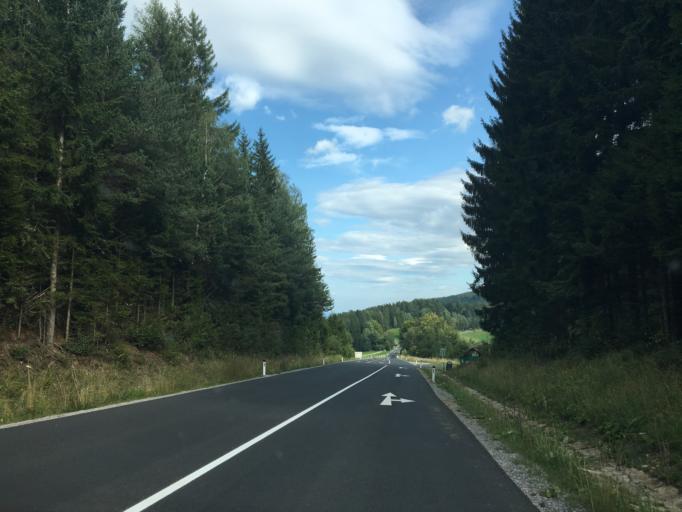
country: AT
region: Styria
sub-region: Politischer Bezirk Deutschlandsberg
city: Freiland bei Deutschlandsberg
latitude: 46.8306
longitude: 15.1104
